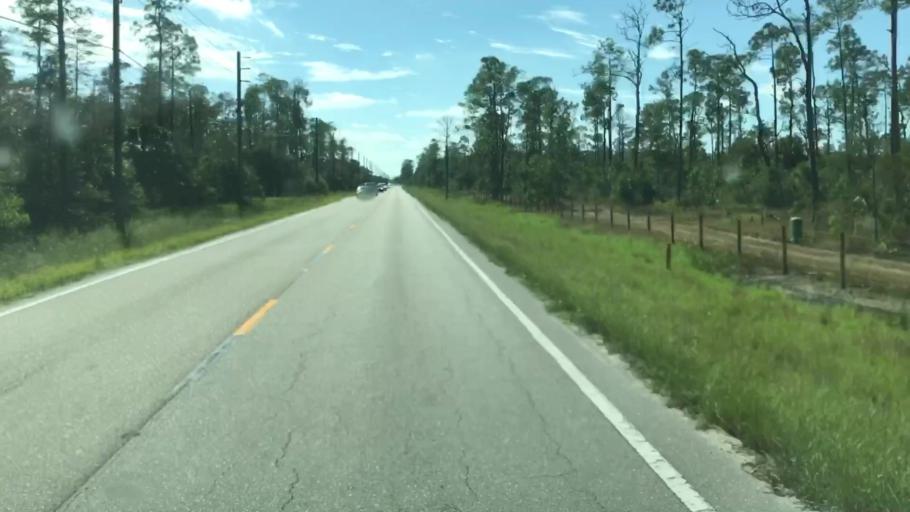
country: US
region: Florida
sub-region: Lee County
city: Bonita Springs
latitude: 26.3434
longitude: -81.7387
